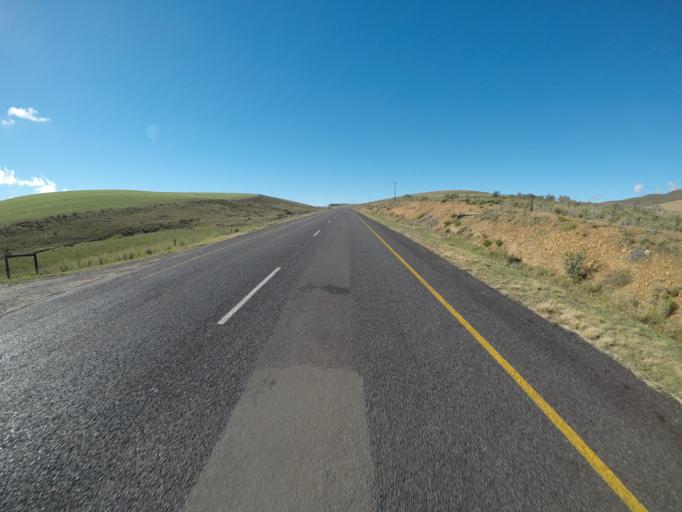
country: ZA
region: Western Cape
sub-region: Overberg District Municipality
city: Caledon
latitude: -34.1482
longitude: 19.4862
